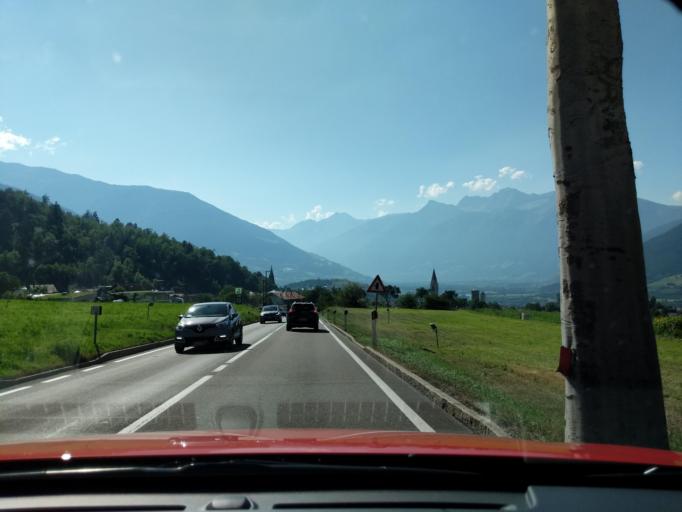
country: IT
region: Trentino-Alto Adige
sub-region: Bolzano
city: Malles Venosta
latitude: 46.6956
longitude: 10.5378
